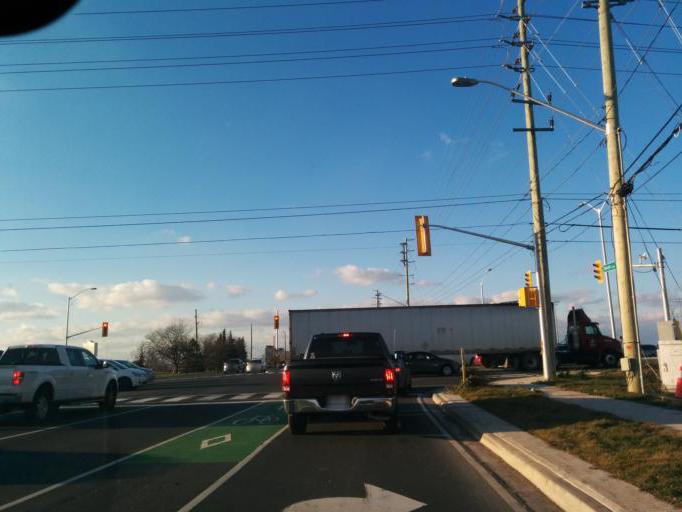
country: CA
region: Ontario
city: Oakville
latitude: 43.5080
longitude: -79.6968
